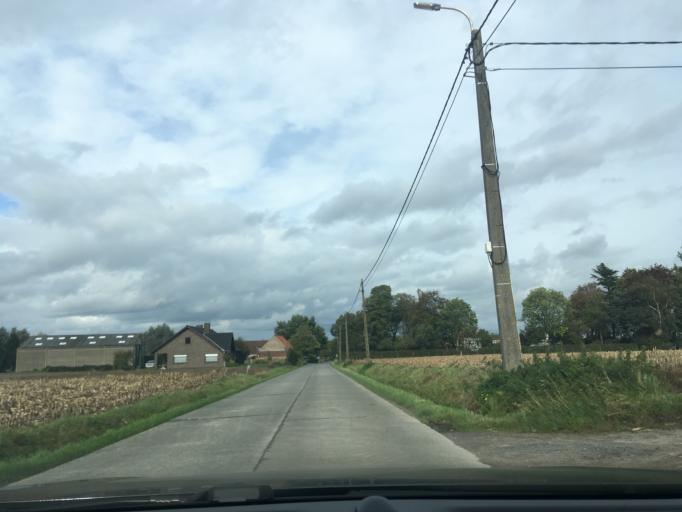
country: BE
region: Flanders
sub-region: Provincie West-Vlaanderen
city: Roeselare
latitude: 50.9230
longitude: 3.1070
